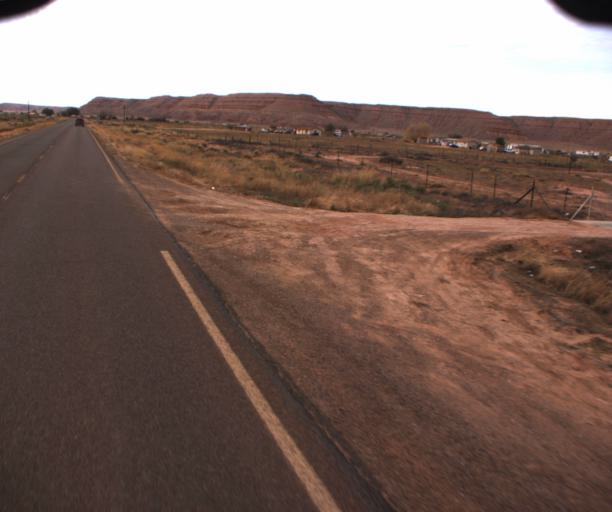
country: US
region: Arizona
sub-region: Apache County
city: Many Farms
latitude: 36.2582
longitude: -109.6037
